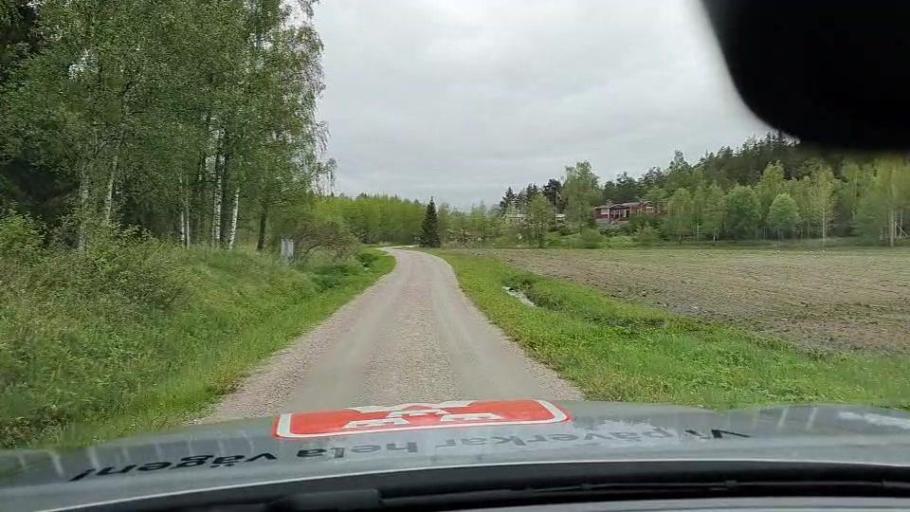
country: SE
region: Soedermanland
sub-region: Nykopings Kommun
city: Svalsta
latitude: 58.6207
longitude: 16.9382
